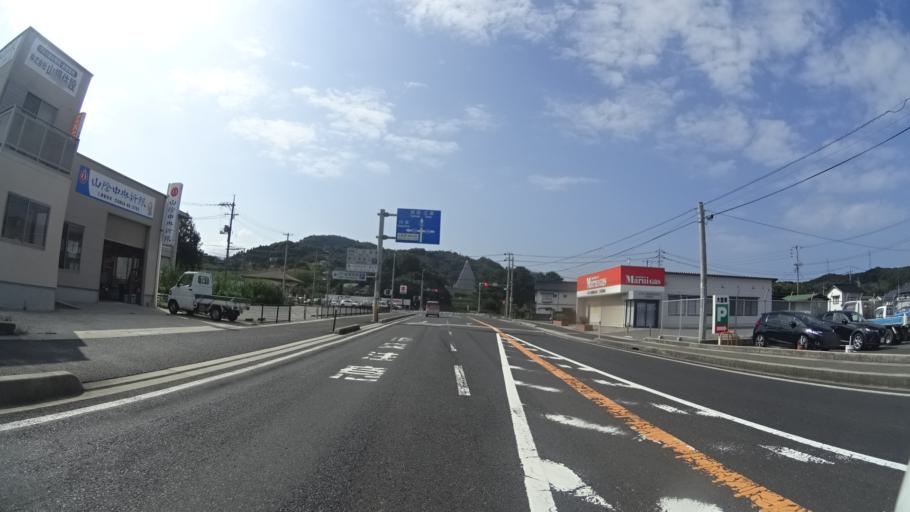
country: JP
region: Shimane
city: Odacho-oda
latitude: 35.1491
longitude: 132.4051
